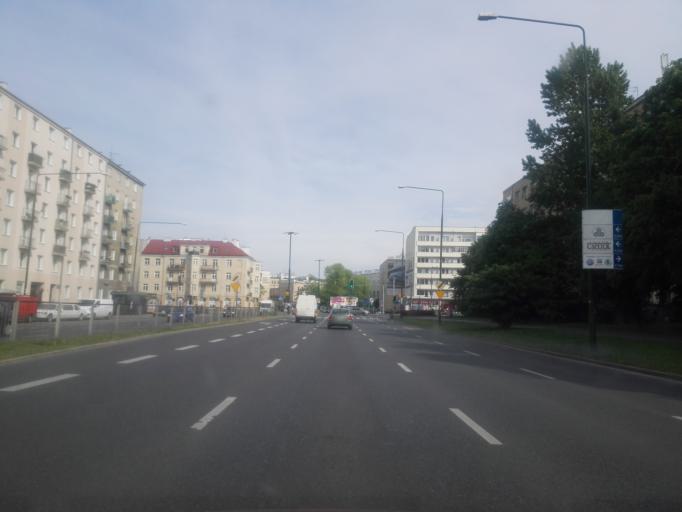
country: PL
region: Masovian Voivodeship
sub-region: Warszawa
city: Ochota
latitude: 52.2167
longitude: 20.9796
